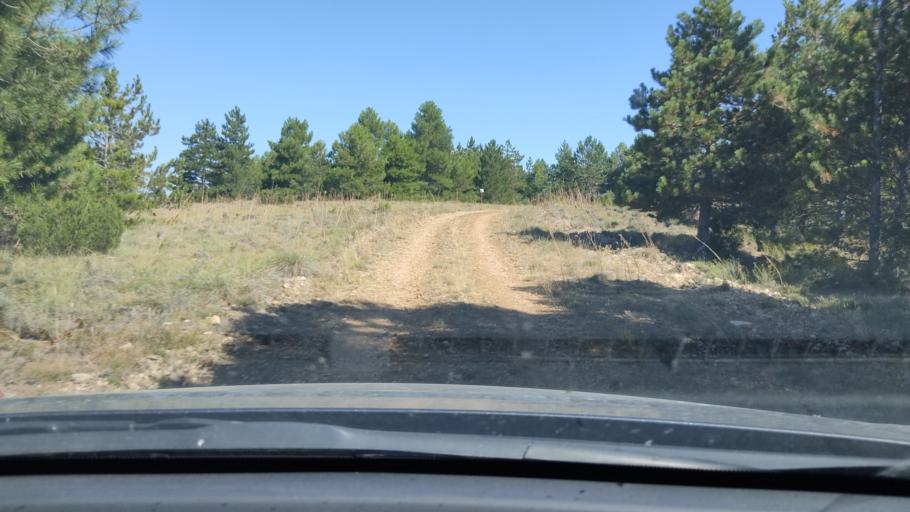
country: ES
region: Aragon
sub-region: Provincia de Teruel
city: Allueva
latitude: 41.0285
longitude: -1.0515
